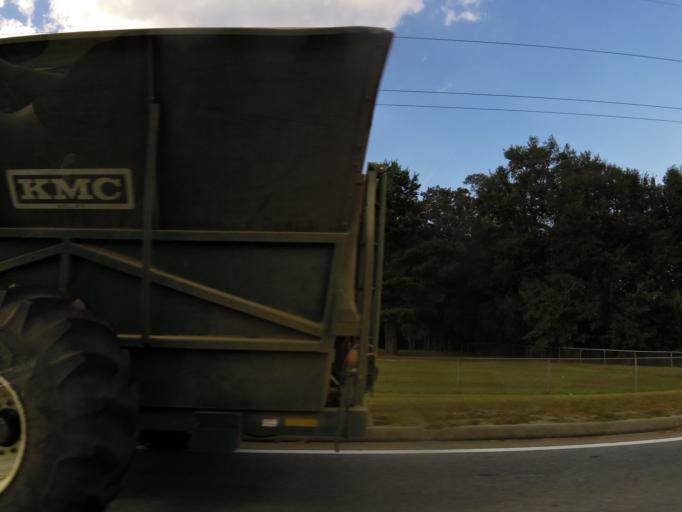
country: US
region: Georgia
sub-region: Brooks County
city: Quitman
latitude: 30.7854
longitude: -83.5337
